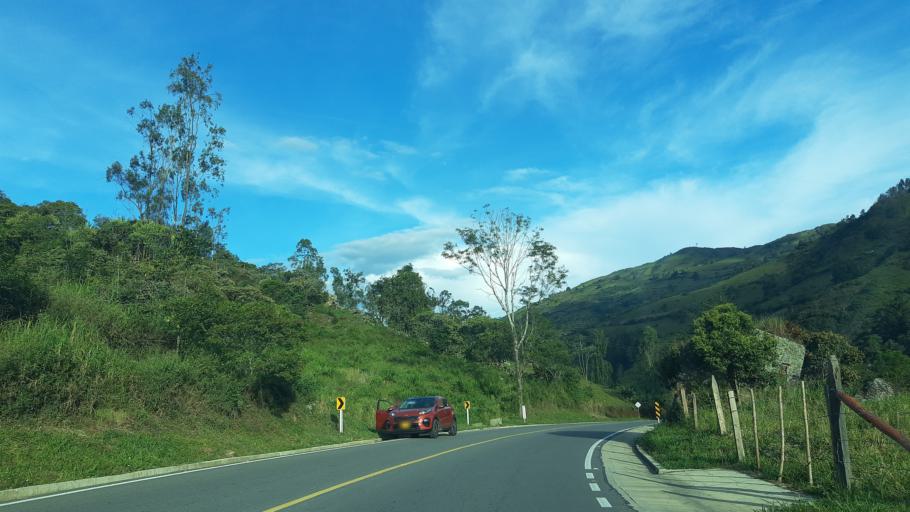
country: CO
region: Cundinamarca
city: Macheta
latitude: 5.0733
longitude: -73.5990
